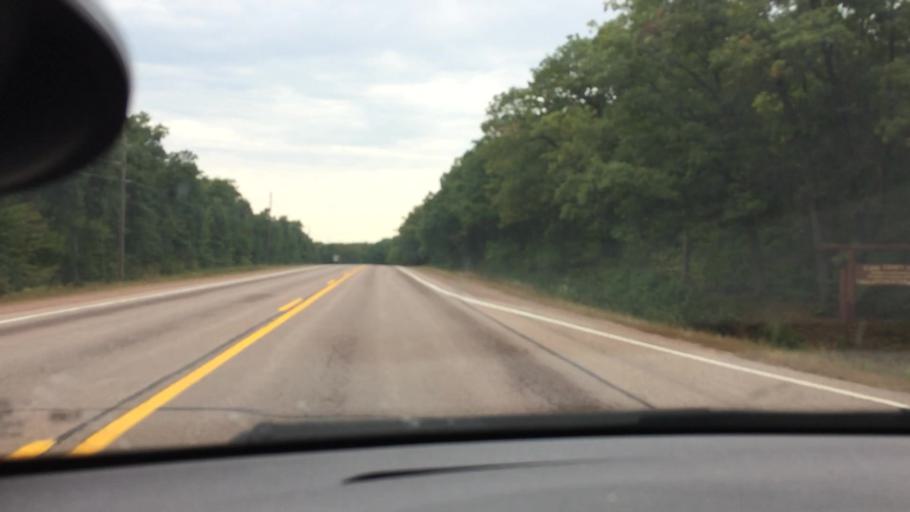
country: US
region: Wisconsin
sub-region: Clark County
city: Neillsville
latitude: 44.5810
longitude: -90.7413
